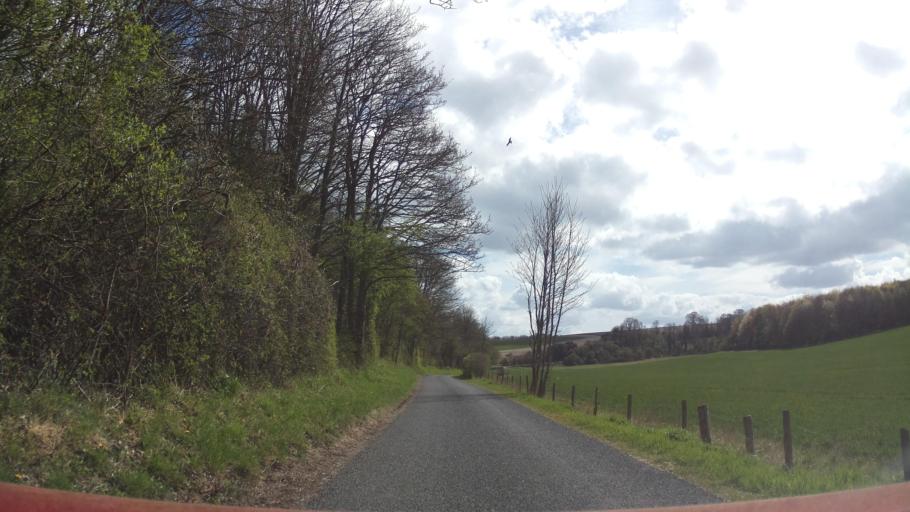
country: GB
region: England
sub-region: West Berkshire
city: Kintbury
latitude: 51.3293
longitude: -1.4682
